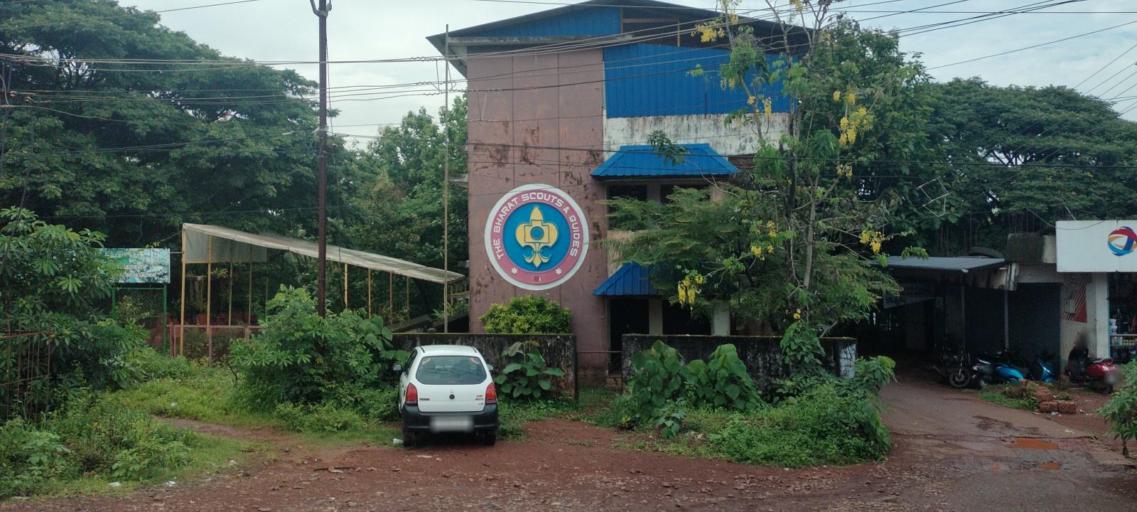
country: IN
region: Kerala
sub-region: Kasaragod District
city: Kasaragod
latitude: 12.5152
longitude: 75.0083
